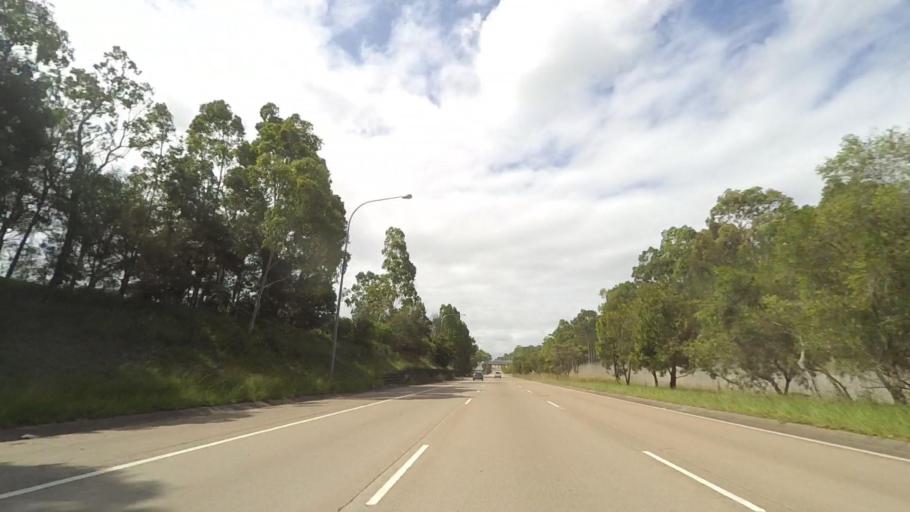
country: AU
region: New South Wales
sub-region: Newcastle
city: North Lambton
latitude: -32.9011
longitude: 151.6938
